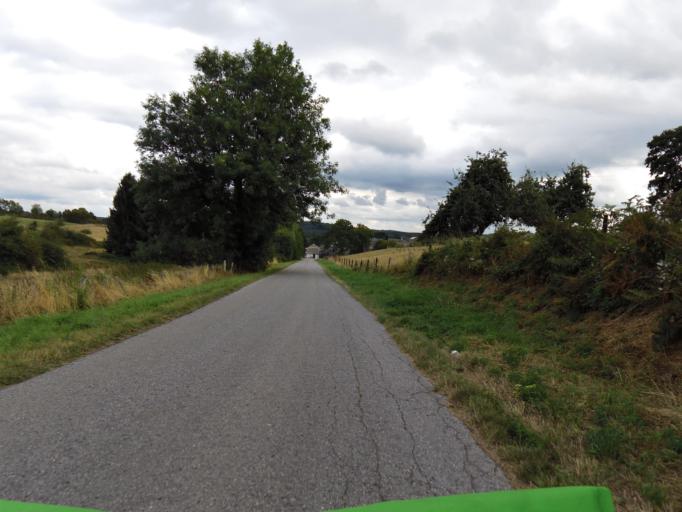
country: BE
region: Wallonia
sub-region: Province de Namur
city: Bievre
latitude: 49.9091
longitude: 4.9876
